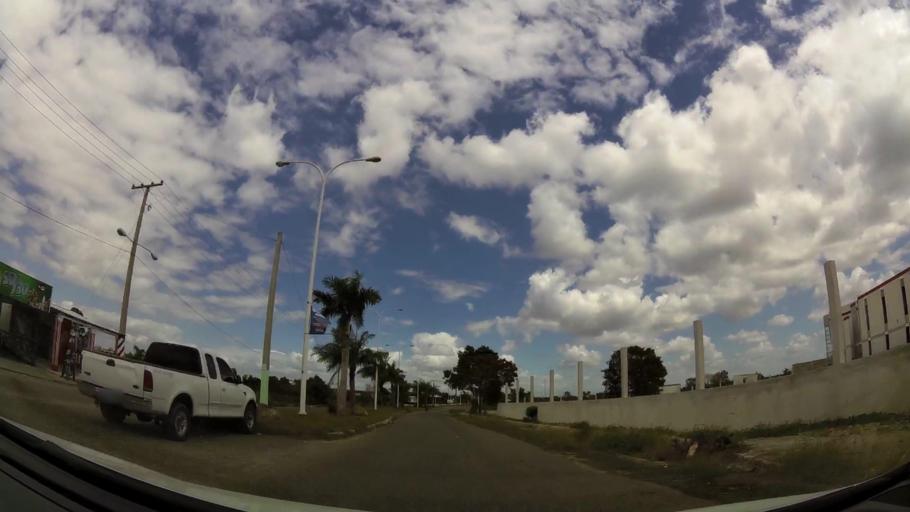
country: DO
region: Santo Domingo
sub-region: Santo Domingo
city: Boca Chica
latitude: 18.4564
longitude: -69.6617
